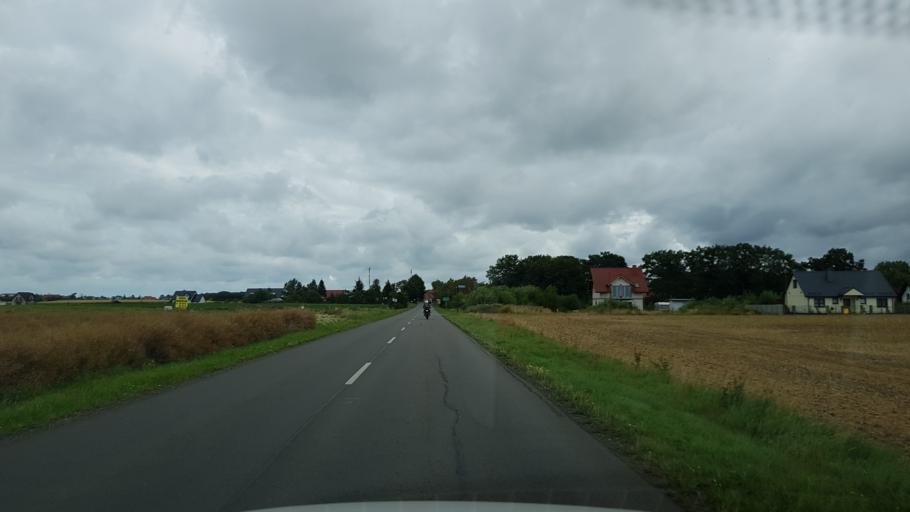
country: PL
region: West Pomeranian Voivodeship
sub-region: Powiat gryficki
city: Rewal
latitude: 54.0681
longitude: 15.0299
